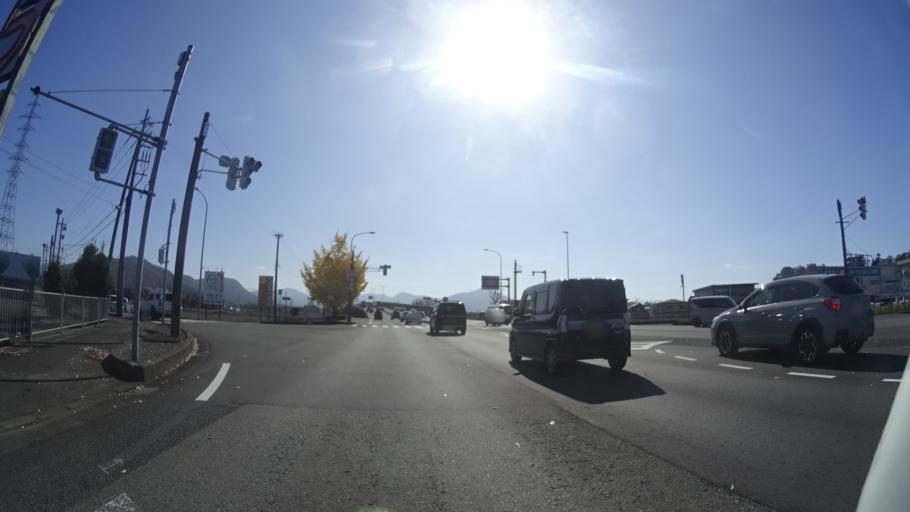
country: JP
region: Fukui
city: Sabae
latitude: 35.9562
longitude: 136.1888
